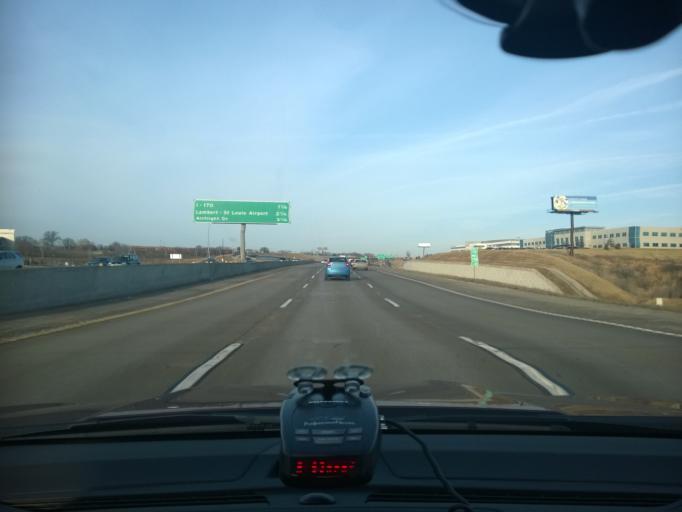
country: US
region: Missouri
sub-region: Saint Louis County
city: Cool Valley
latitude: 38.7209
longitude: -90.3092
